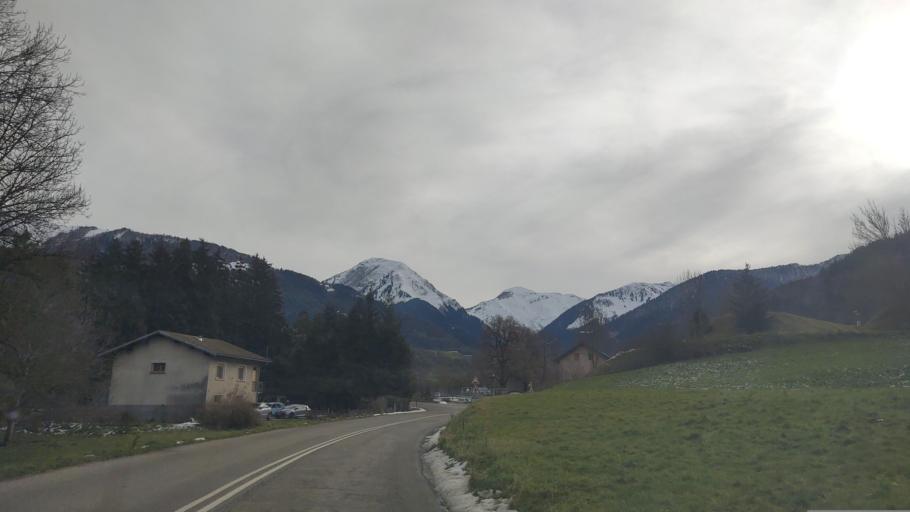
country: FR
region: Rhone-Alpes
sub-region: Departement de la Savoie
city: Gresy-sur-Isere
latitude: 45.6678
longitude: 6.1559
